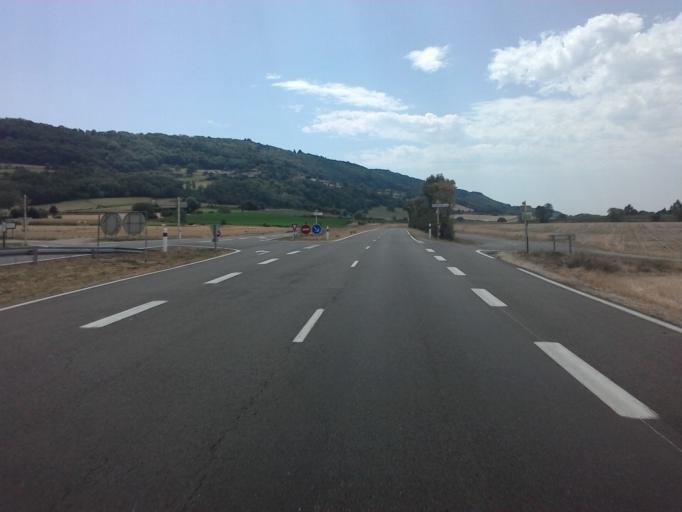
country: FR
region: Franche-Comte
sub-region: Departement du Jura
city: Saint-Amour
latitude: 46.4170
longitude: 5.3512
